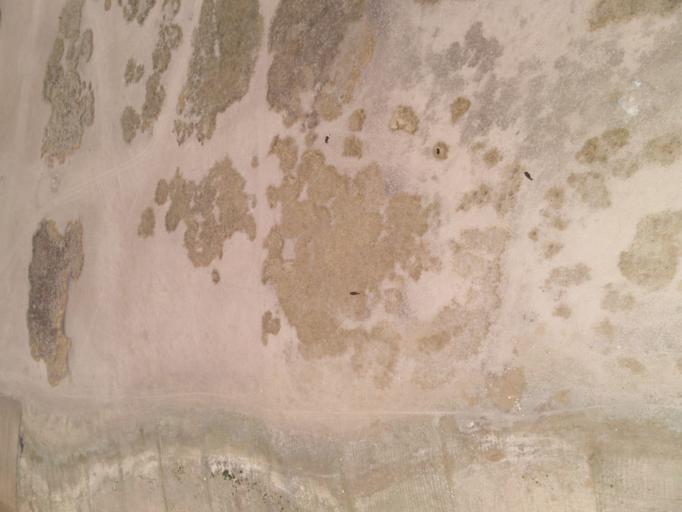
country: BO
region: La Paz
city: Batallas
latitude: -16.3522
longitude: -68.6296
